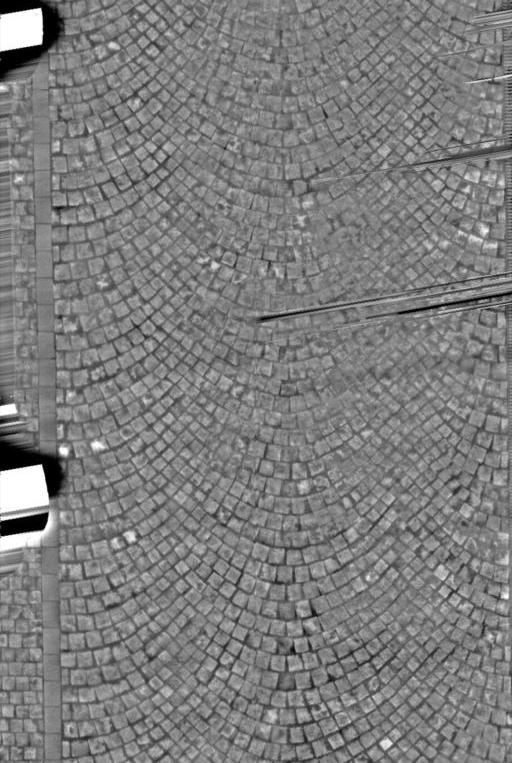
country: US
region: Washington, D.C.
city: Washington, D.C.
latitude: 38.8788
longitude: -77.0246
